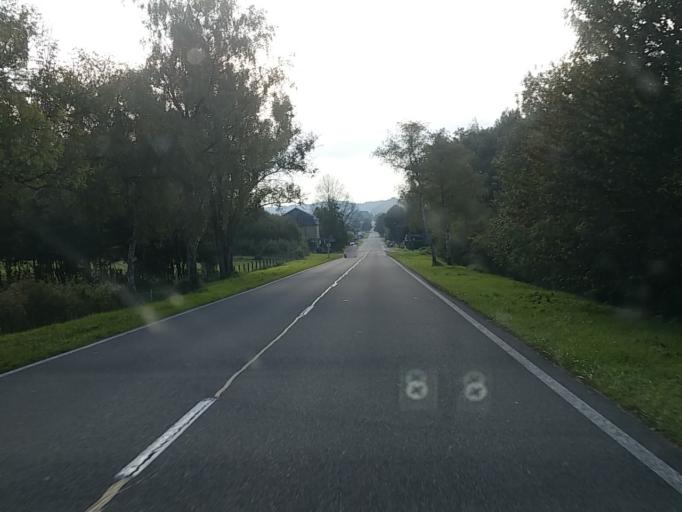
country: BE
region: Wallonia
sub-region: Province du Luxembourg
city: Herbeumont
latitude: 49.7293
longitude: 5.2351
